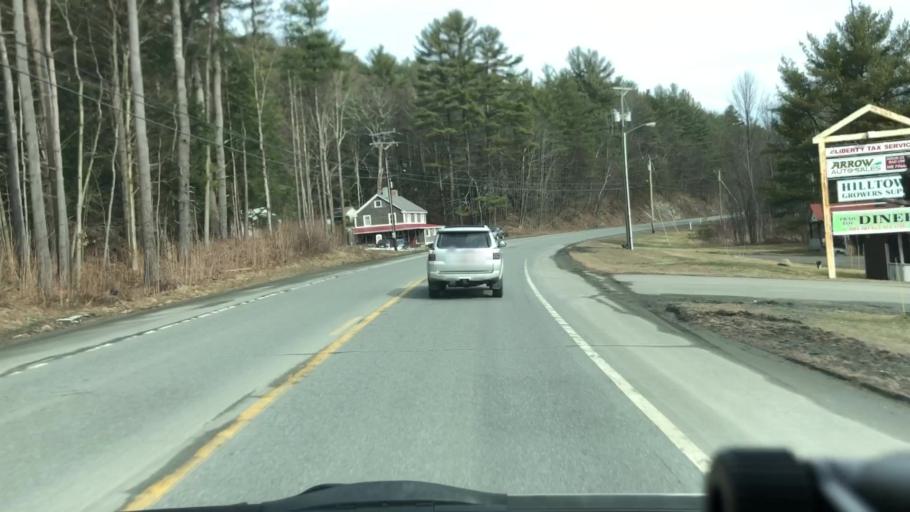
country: US
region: Massachusetts
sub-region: Franklin County
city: Shelburne
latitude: 42.6034
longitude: -72.6722
